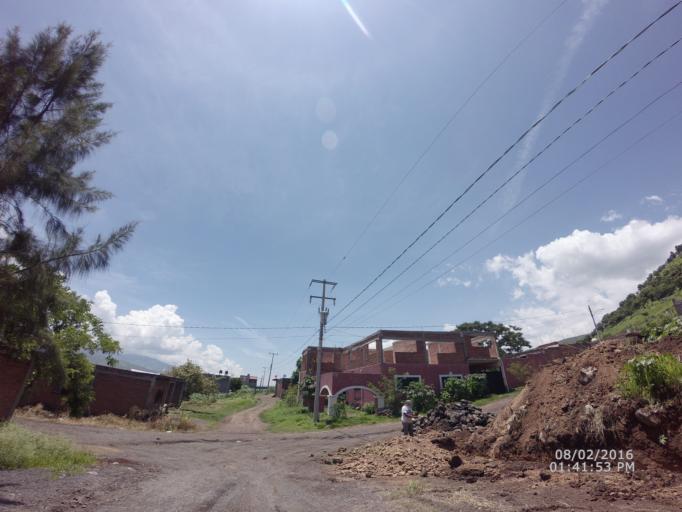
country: MX
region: Nayarit
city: Ixtlan del Rio
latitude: 21.0319
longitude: -104.3574
